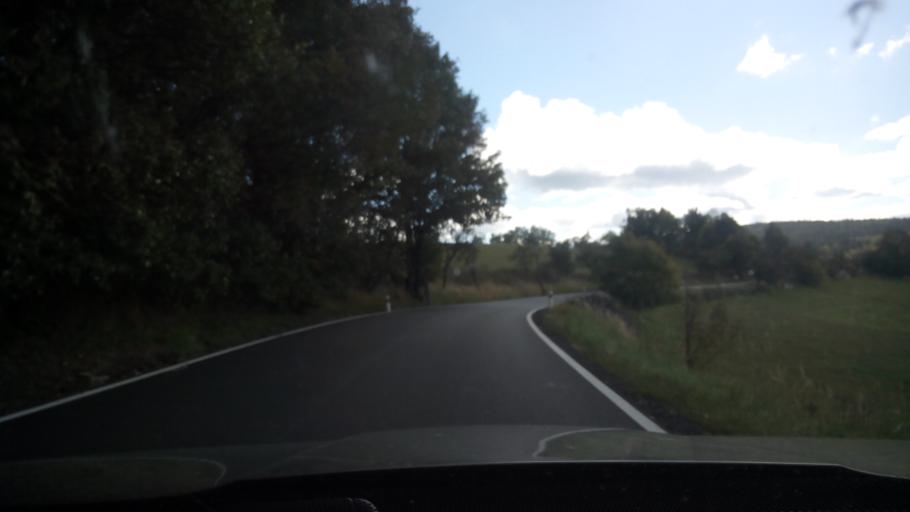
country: CZ
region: Plzensky
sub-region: Okres Klatovy
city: Kasperske Hory
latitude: 49.1294
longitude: 13.6132
